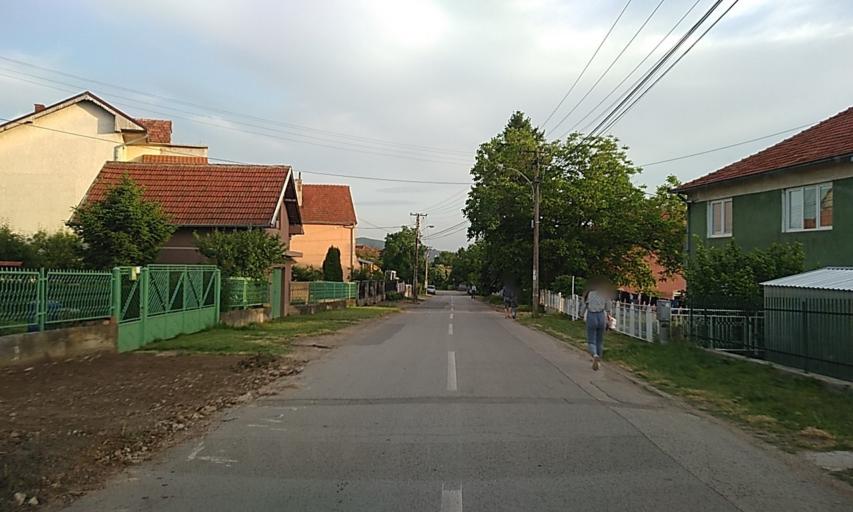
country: RS
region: Central Serbia
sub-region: Nisavski Okrug
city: Nis
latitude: 43.2963
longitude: 21.8661
